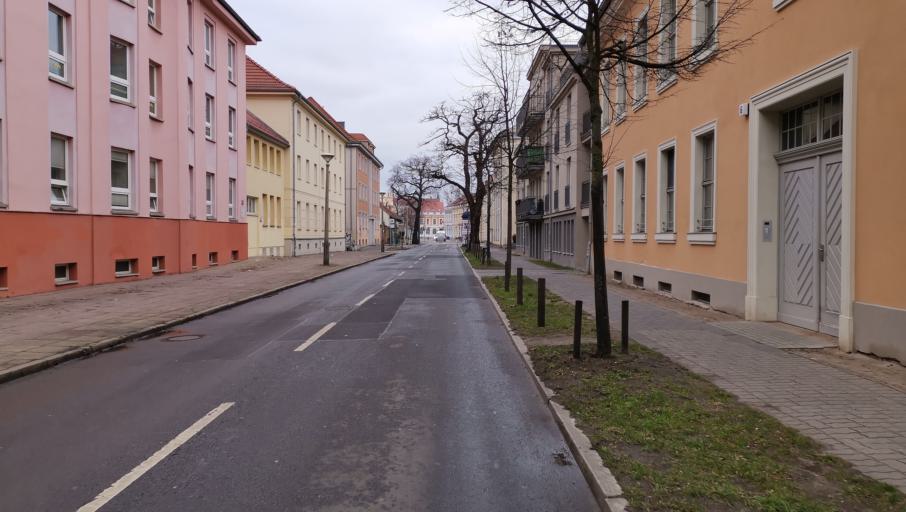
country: DE
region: Brandenburg
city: Potsdam
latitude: 52.3972
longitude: 13.0485
